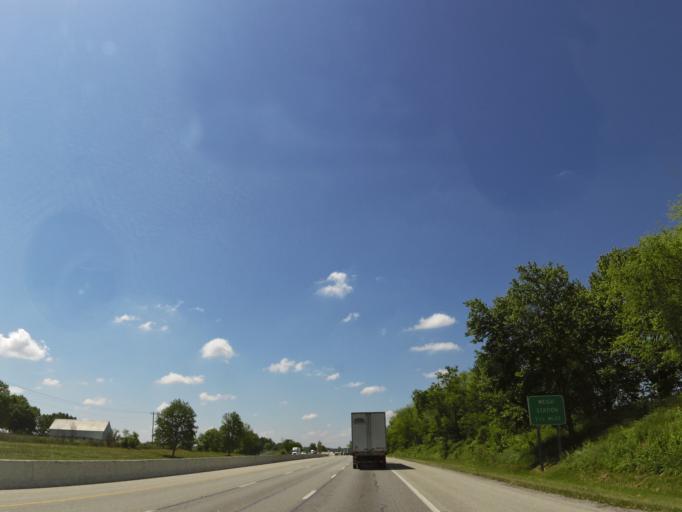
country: US
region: Kentucky
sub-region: Laurel County
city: London
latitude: 37.0693
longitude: -84.0991
